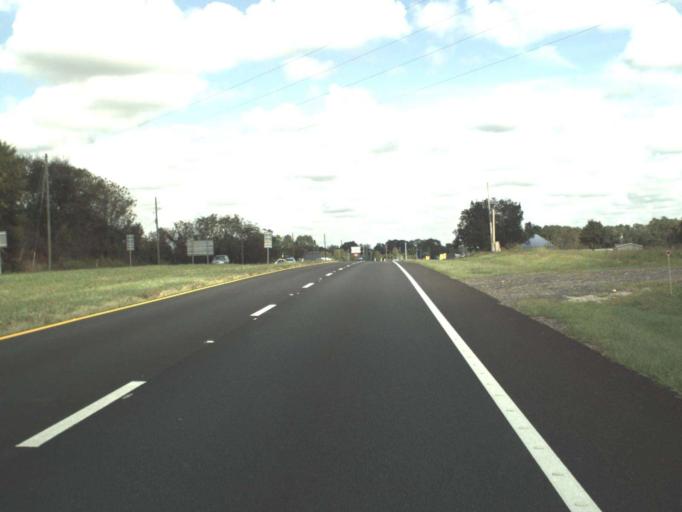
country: US
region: Florida
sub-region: Jackson County
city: Graceville
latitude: 30.9880
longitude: -85.4075
